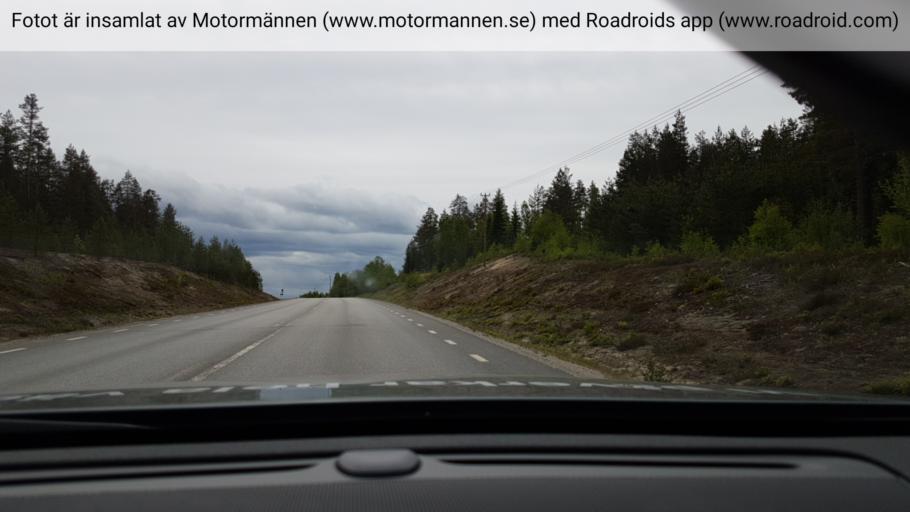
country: SE
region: Vaesterbotten
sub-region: Vannas Kommun
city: Vaennaes
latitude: 64.0331
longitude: 19.6912
